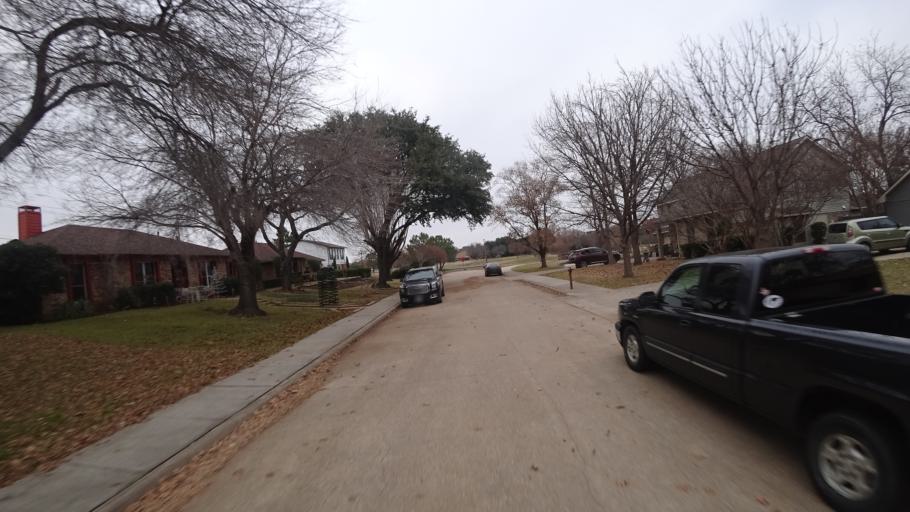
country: US
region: Texas
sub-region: Denton County
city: Highland Village
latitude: 33.0551
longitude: -97.0439
